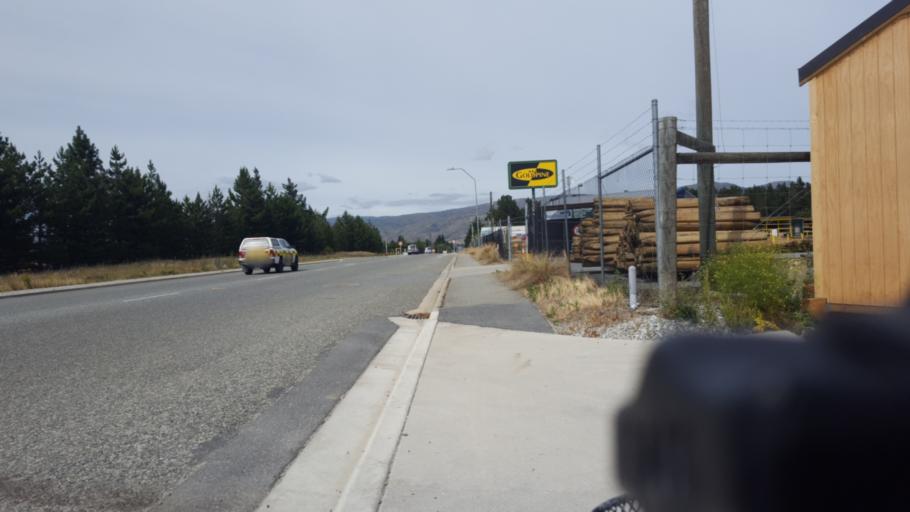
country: NZ
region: Otago
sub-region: Queenstown-Lakes District
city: Wanaka
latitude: -45.0536
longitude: 169.1946
